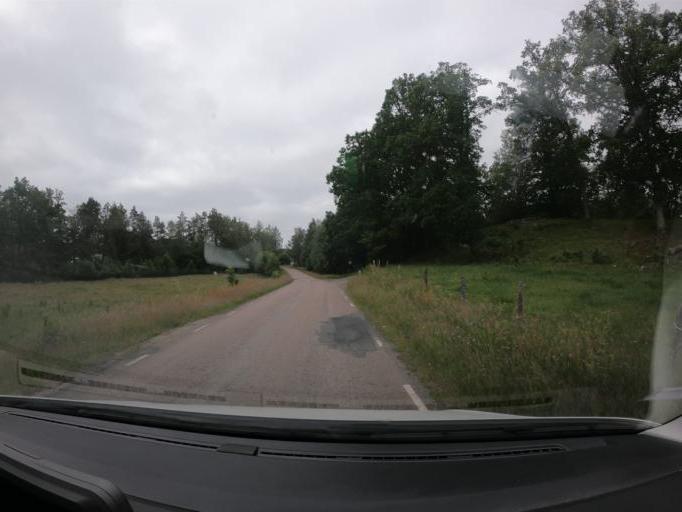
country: SE
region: Skane
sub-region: Perstorps Kommun
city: Perstorp
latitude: 56.1087
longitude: 13.3516
